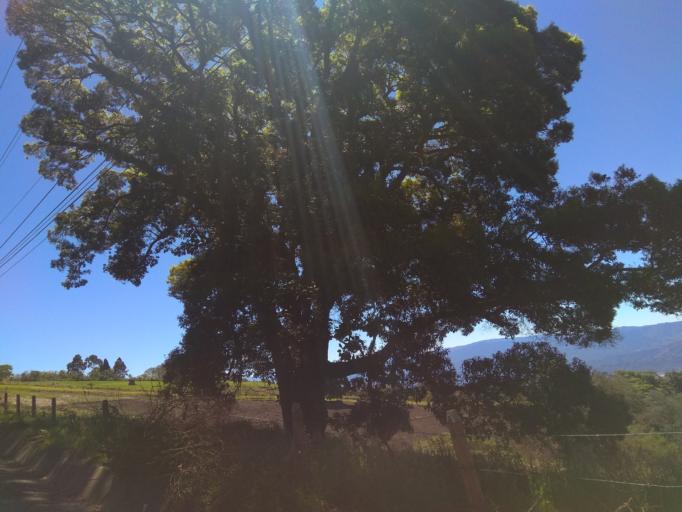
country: CR
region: Cartago
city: Tres Rios
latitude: 9.9422
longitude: -83.9298
